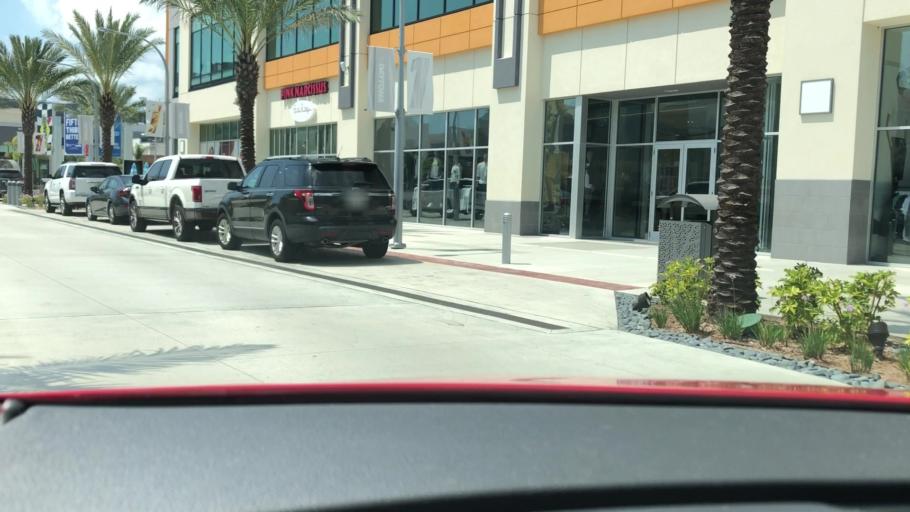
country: US
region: Florida
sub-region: Volusia County
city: Daytona Beach
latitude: 29.1947
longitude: -81.0724
